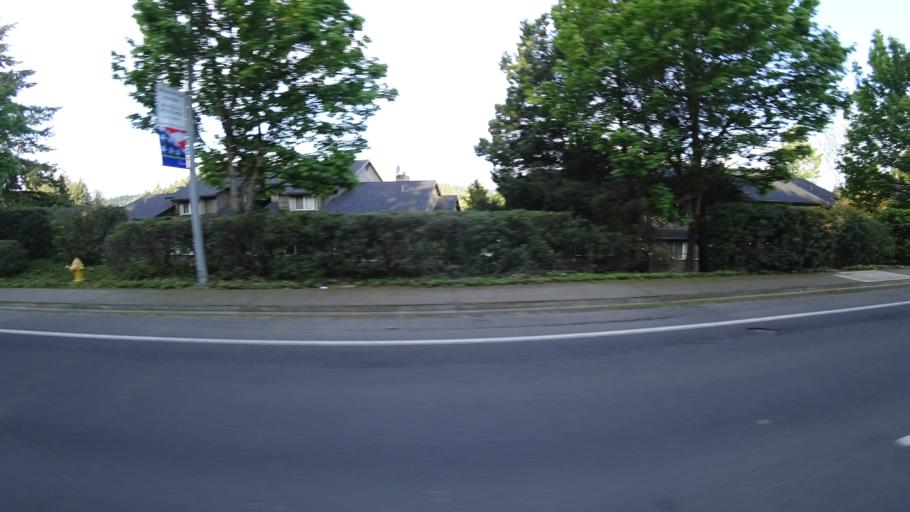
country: US
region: Oregon
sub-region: Washington County
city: Beaverton
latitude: 45.4519
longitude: -122.8261
